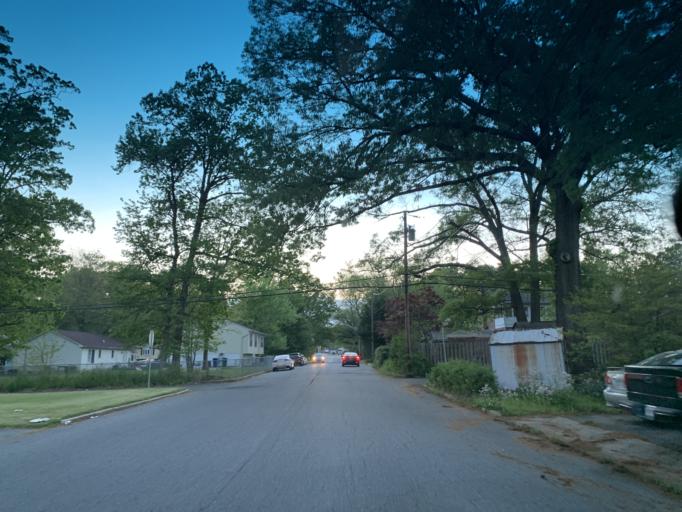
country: US
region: Maryland
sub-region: Harford County
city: Aberdeen
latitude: 39.5052
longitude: -76.1706
